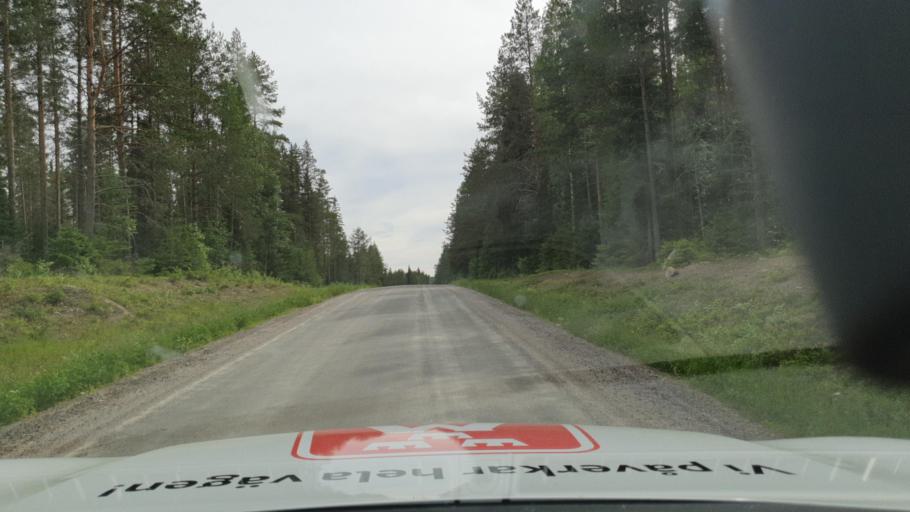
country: SE
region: Vaesterbotten
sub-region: Skelleftea Kommun
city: Burea
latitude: 64.4238
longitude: 21.0116
